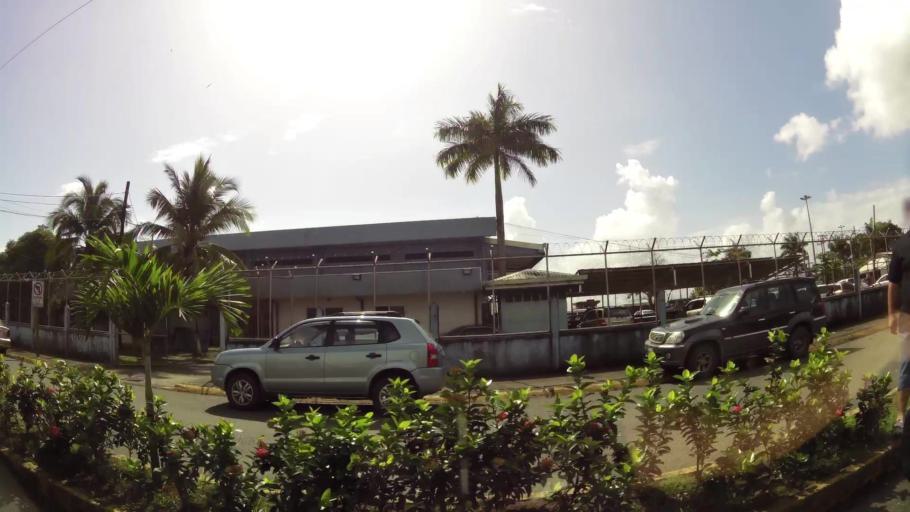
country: CR
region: Limon
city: Limon
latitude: 9.9915
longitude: -83.0273
